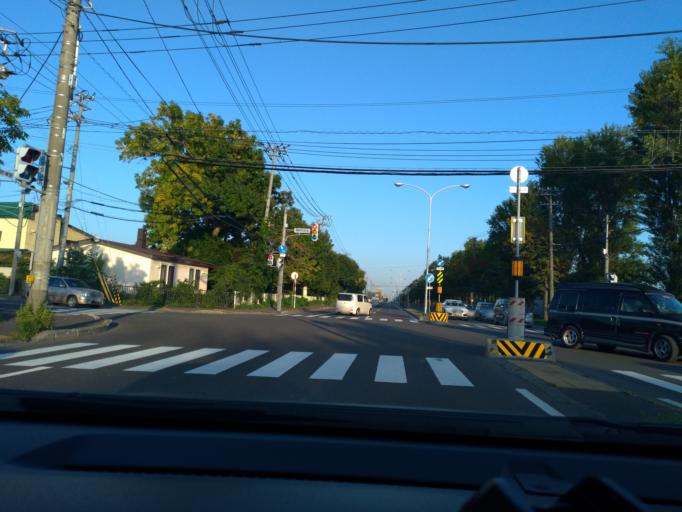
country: JP
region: Hokkaido
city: Ishikari
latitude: 43.1602
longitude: 141.3749
